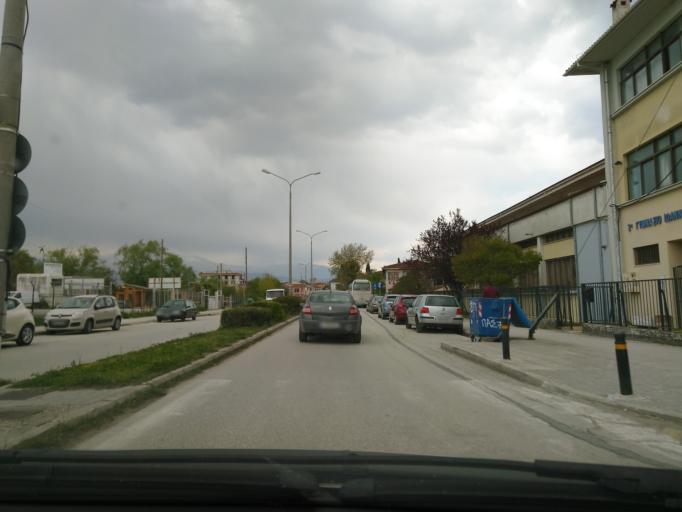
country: GR
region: Epirus
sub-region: Nomos Ioanninon
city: Ioannina
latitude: 39.6721
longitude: 20.8518
